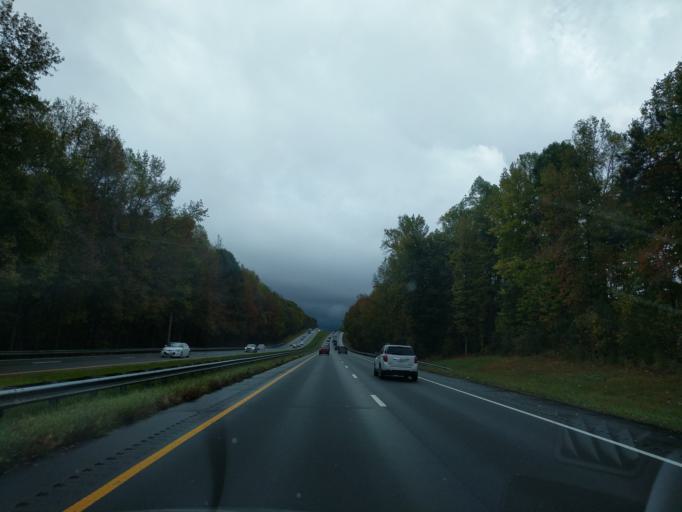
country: US
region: North Carolina
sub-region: Orange County
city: Hillsborough
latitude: 36.0495
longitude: -79.0551
